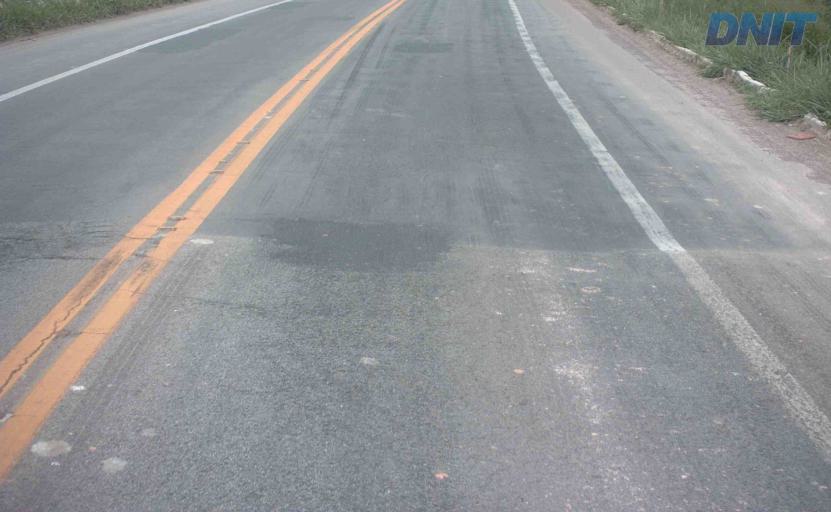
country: BR
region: Minas Gerais
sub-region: Barao De Cocais
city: Barao de Cocais
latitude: -19.7423
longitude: -43.5050
